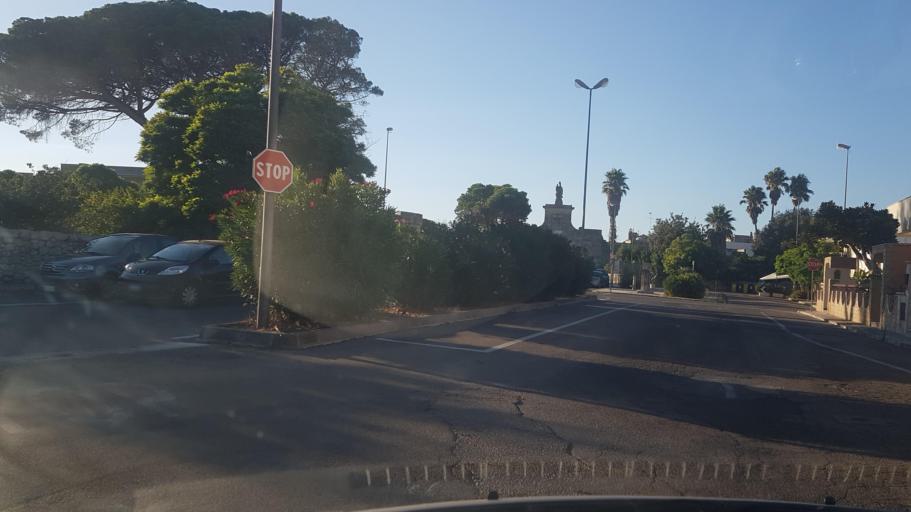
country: IT
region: Apulia
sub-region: Provincia di Lecce
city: Struda
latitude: 40.3327
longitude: 18.2971
